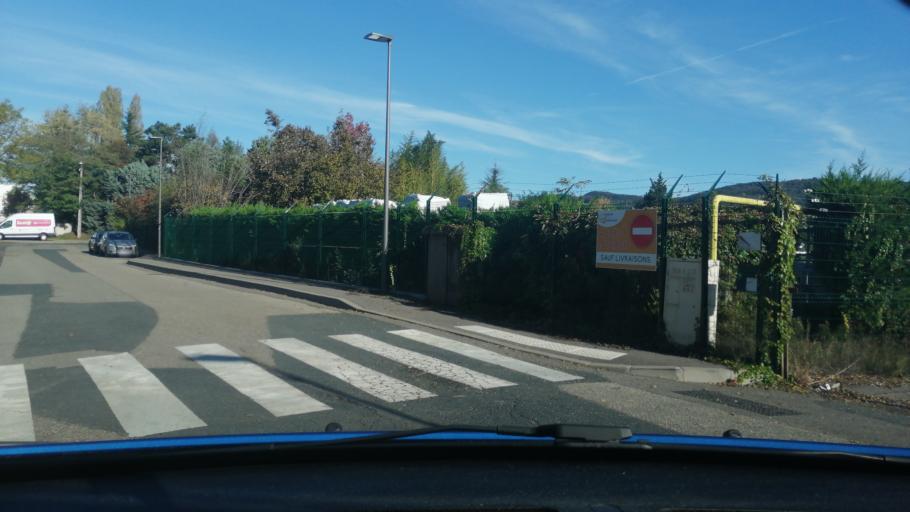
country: FR
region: Rhone-Alpes
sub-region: Departement du Rhone
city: Limonest
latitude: 45.8169
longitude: 4.7704
